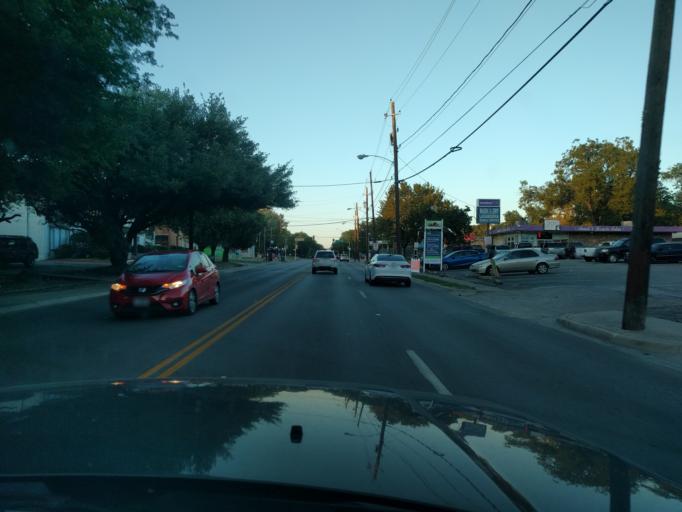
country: US
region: Texas
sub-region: Dallas County
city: Dallas
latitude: 32.7992
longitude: -96.7705
